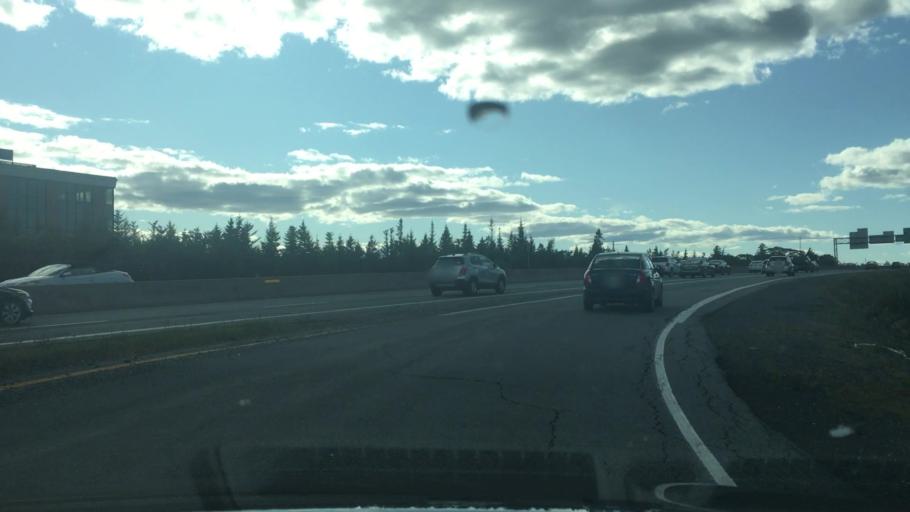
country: CA
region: Nova Scotia
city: Dartmouth
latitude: 44.6446
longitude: -63.6589
